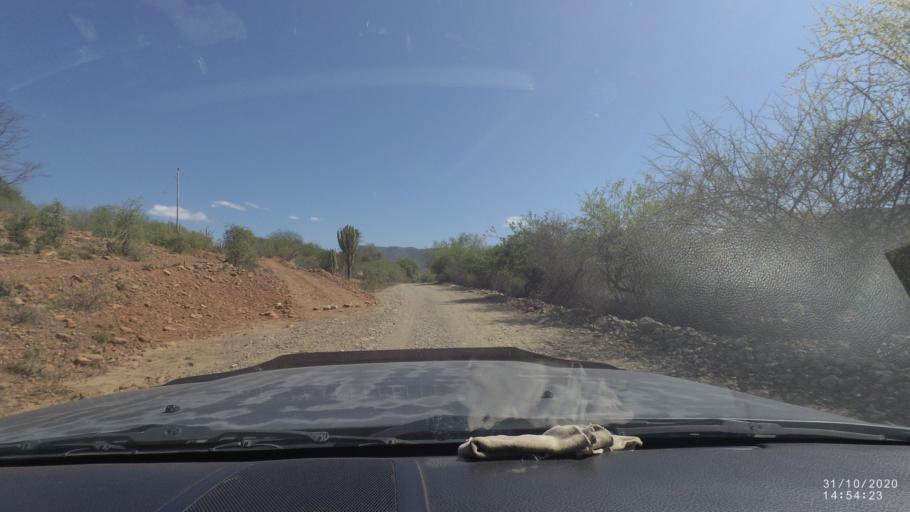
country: BO
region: Cochabamba
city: Aiquile
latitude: -18.2257
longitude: -64.8575
